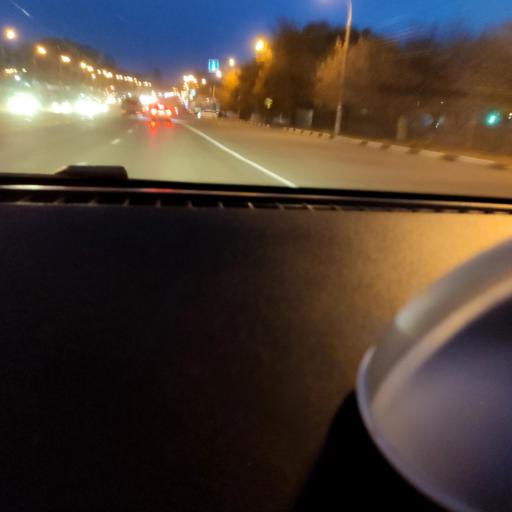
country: RU
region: Samara
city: Smyshlyayevka
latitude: 53.2114
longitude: 50.2722
